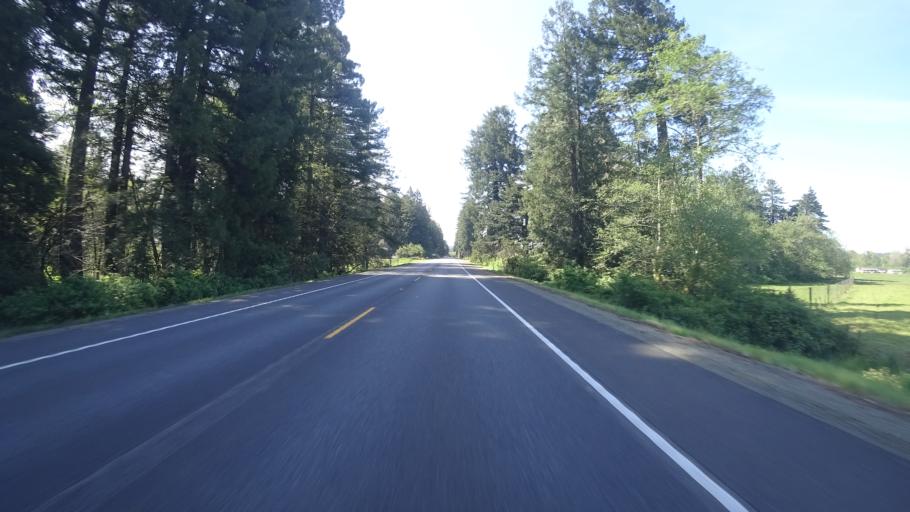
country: US
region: California
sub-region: Del Norte County
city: Bertsch-Oceanview
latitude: 41.8882
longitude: -124.1367
